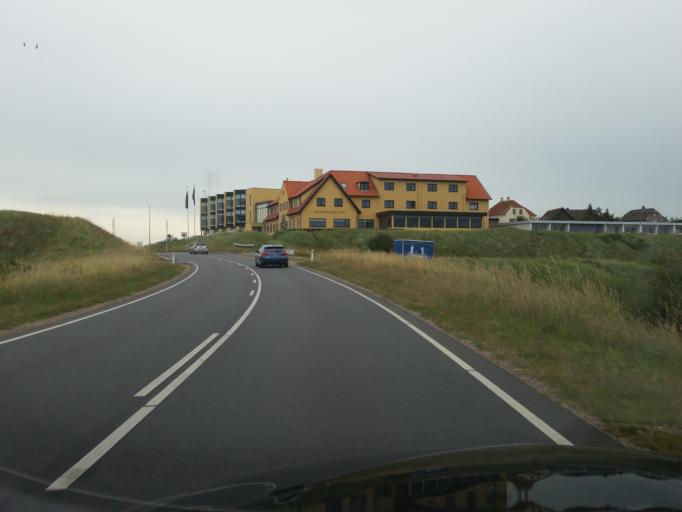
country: DK
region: Central Jutland
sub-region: Ringkobing-Skjern Kommune
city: Hvide Sande
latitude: 55.8172
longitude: 8.1898
